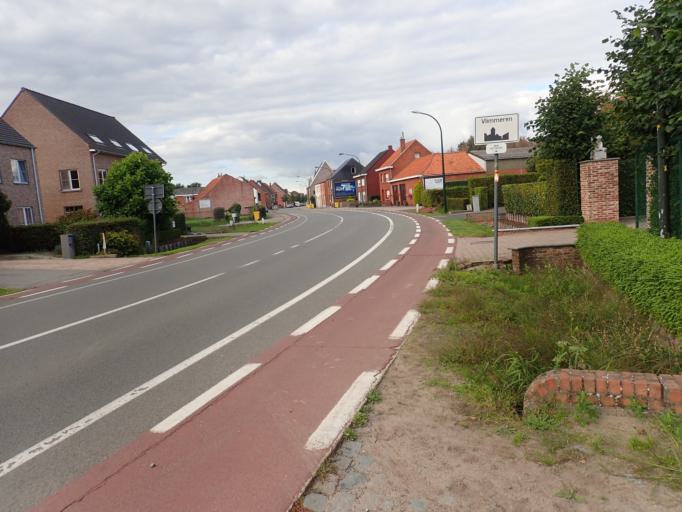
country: BE
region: Flanders
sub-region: Provincie Antwerpen
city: Oostmalle
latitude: 51.2912
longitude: 4.7804
